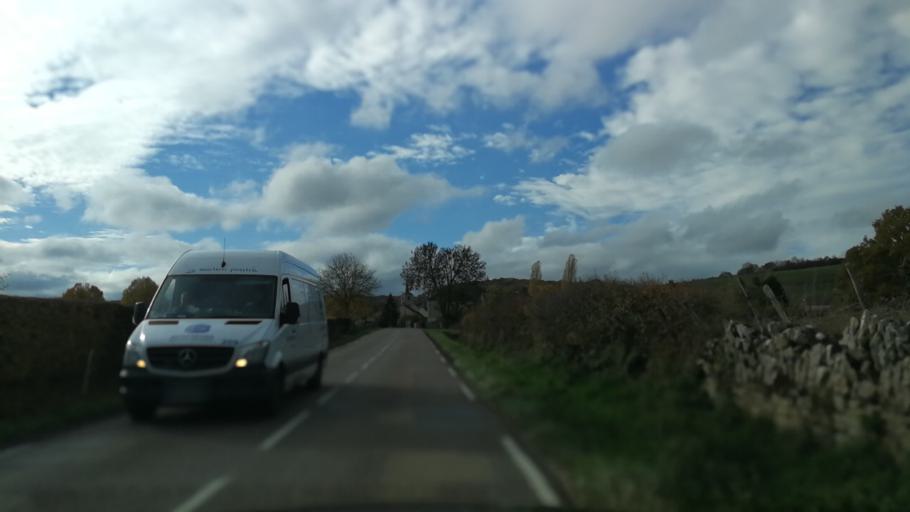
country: FR
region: Bourgogne
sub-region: Departement de la Cote-d'Or
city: Pouilly-en-Auxois
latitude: 47.2753
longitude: 4.4928
